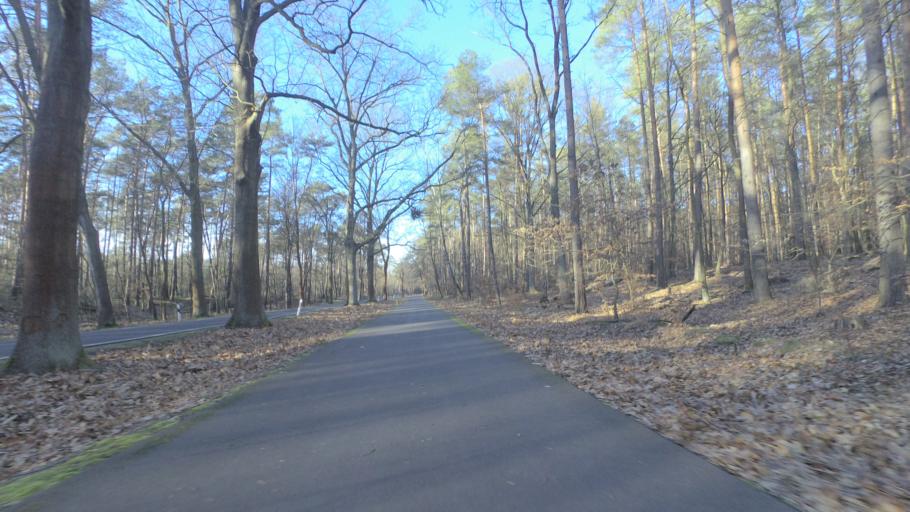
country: DE
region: Brandenburg
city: Ihlow
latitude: 52.0069
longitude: 13.3222
